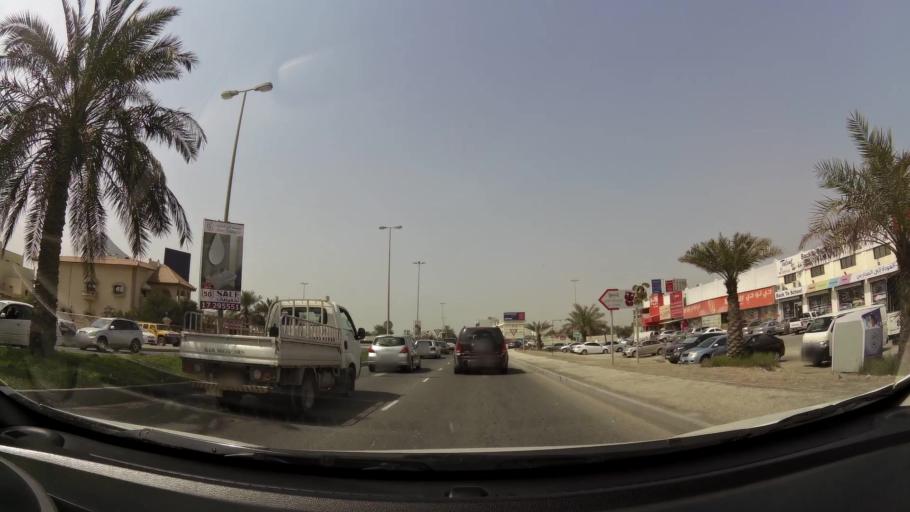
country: BH
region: Manama
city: Jidd Hafs
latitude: 26.2205
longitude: 50.5002
